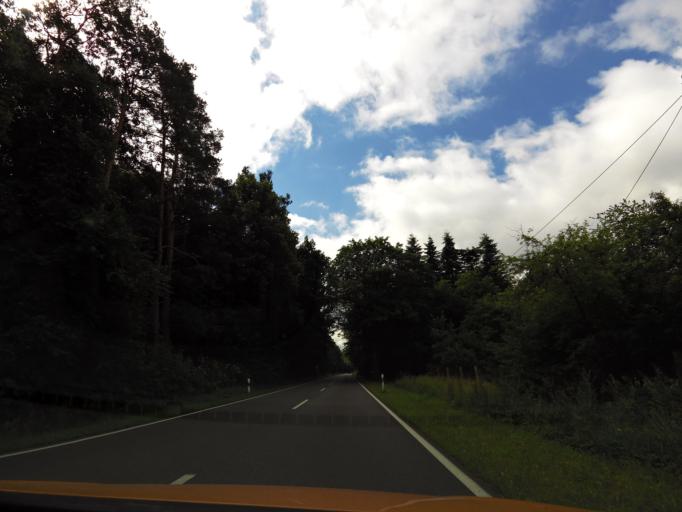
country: DE
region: Mecklenburg-Vorpommern
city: Muhl Rosin
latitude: 53.7651
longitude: 12.2458
